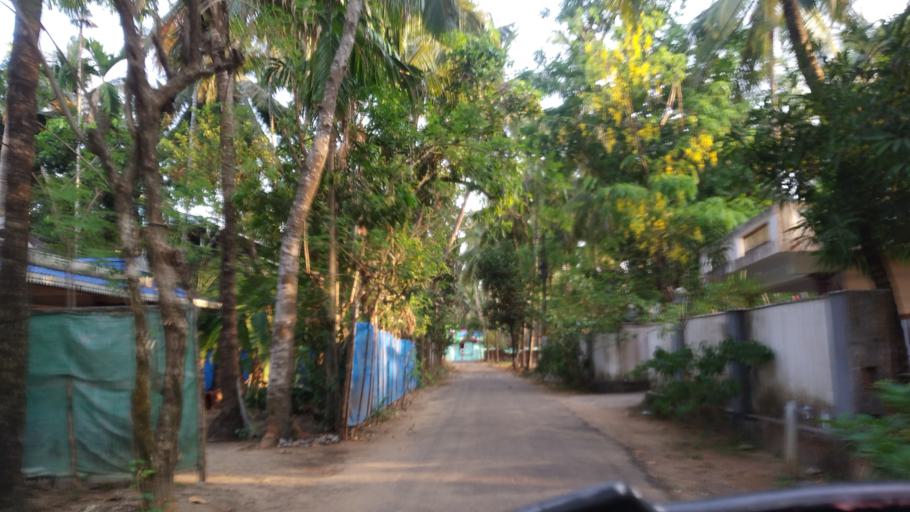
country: IN
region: Kerala
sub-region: Thrissur District
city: Thanniyam
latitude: 10.4092
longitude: 76.0894
